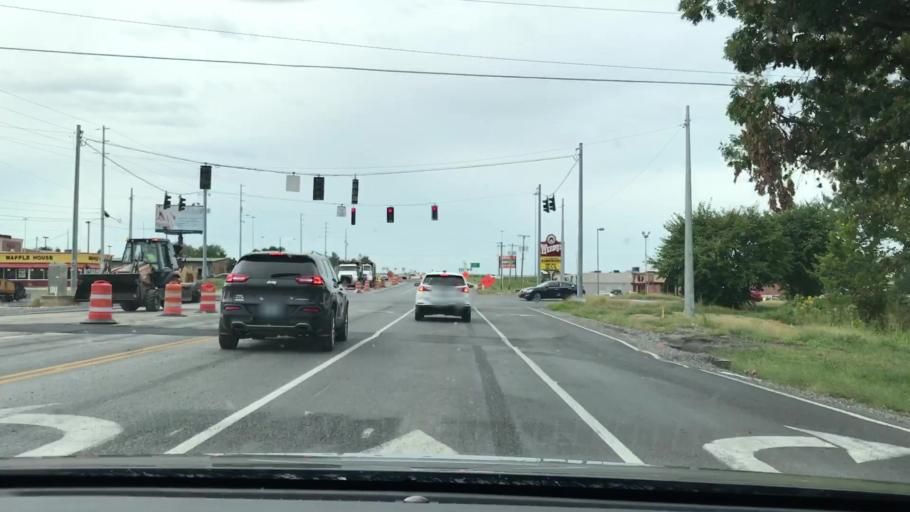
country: US
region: Kentucky
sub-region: Marshall County
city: Benton
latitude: 36.8670
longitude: -88.3596
